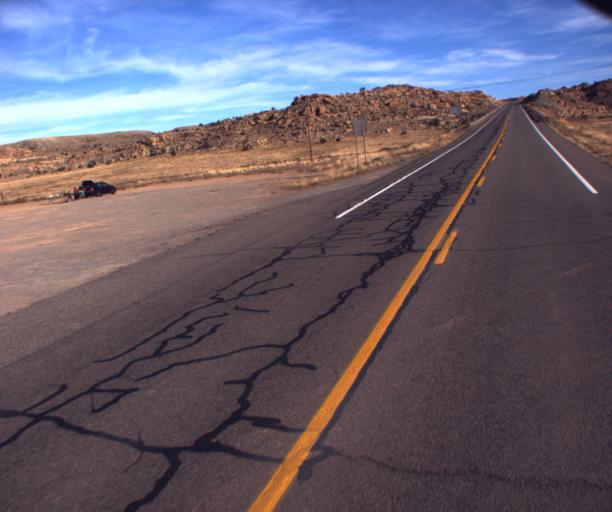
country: US
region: New Mexico
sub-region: San Juan County
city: Shiprock
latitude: 36.9192
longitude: -109.0844
